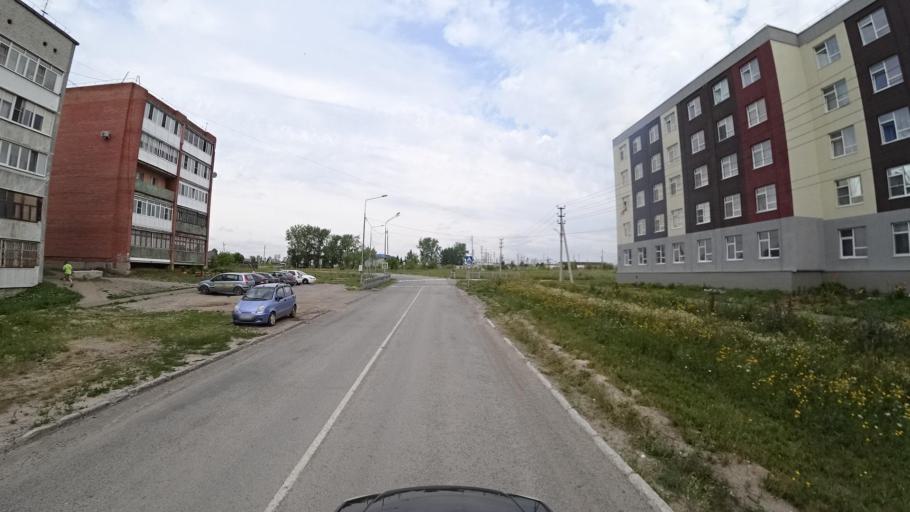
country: RU
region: Sverdlovsk
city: Kamyshlov
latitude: 56.8469
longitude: 62.7451
